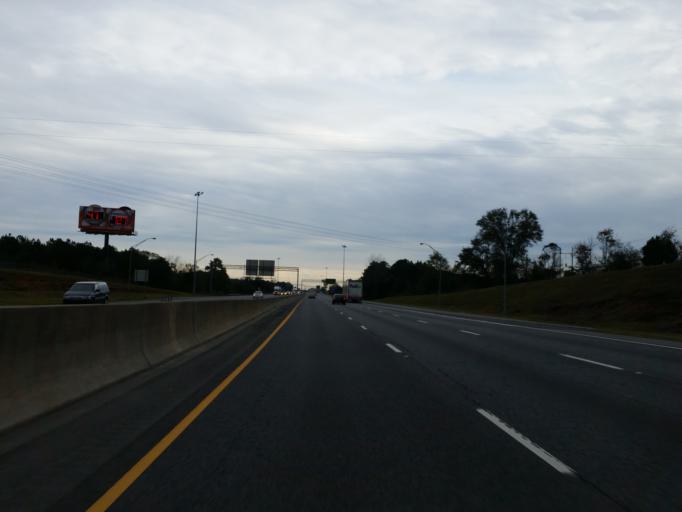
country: US
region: Georgia
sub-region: Tift County
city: Unionville
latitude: 31.4398
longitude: -83.5258
